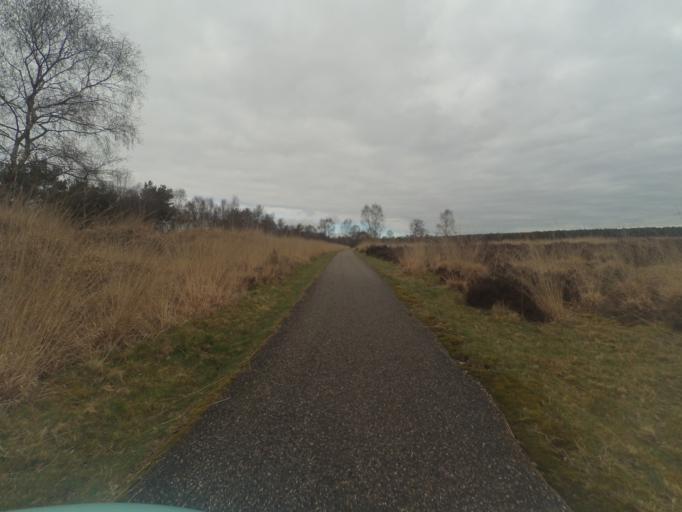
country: NL
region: Gelderland
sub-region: Gemeente Rozendaal
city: Rozendaal
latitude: 52.0343
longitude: 5.9387
